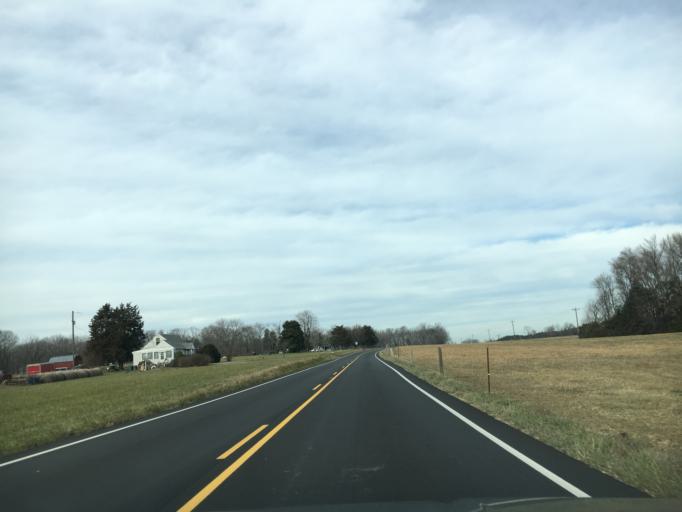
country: US
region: Virginia
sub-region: Goochland County
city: Goochland
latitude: 37.8114
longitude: -77.8682
